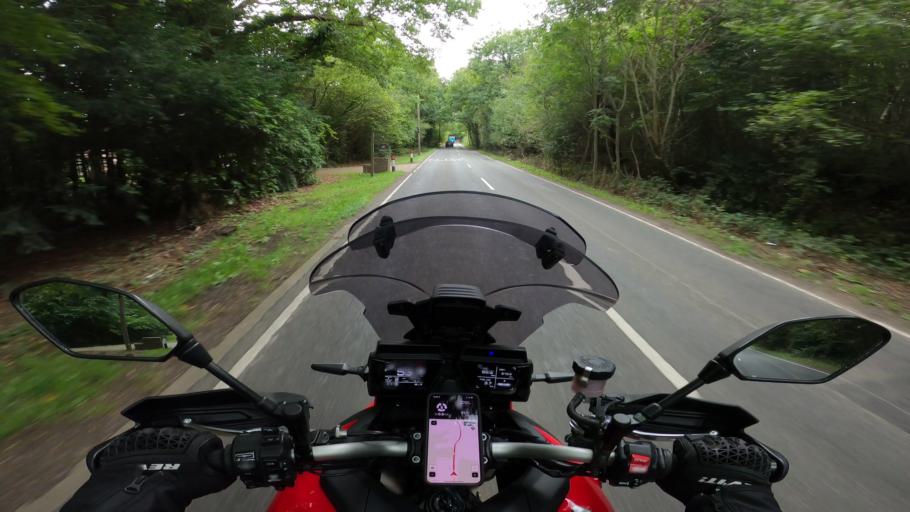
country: GB
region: England
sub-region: West Sussex
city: Crawley Down
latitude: 51.1538
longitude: -0.0743
